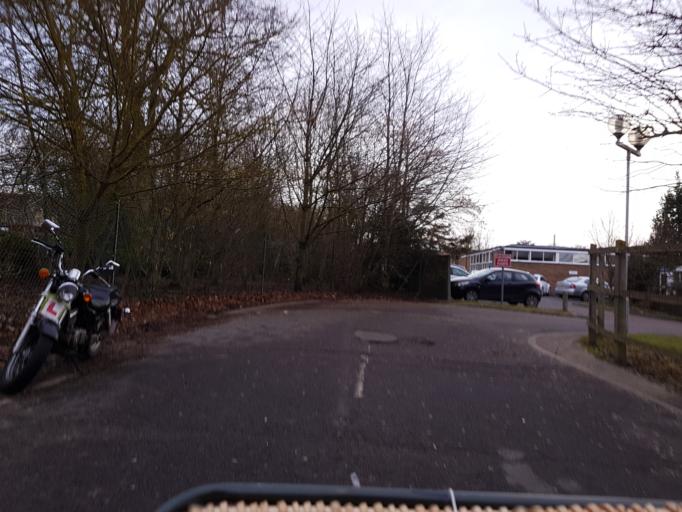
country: GB
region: England
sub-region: Cambridgeshire
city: Fulbourn
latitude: 52.1862
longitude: 0.1906
